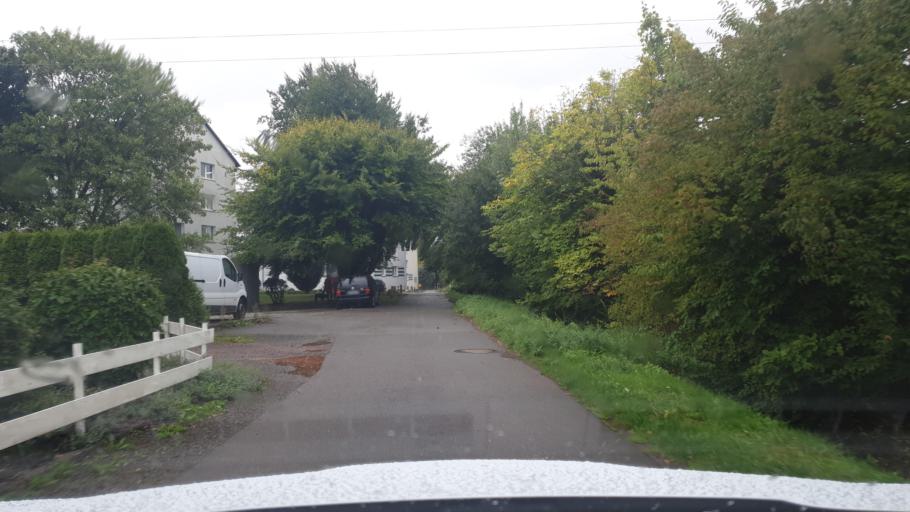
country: DE
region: North Rhine-Westphalia
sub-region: Regierungsbezirk Detmold
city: Minden
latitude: 52.2861
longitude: 8.8810
